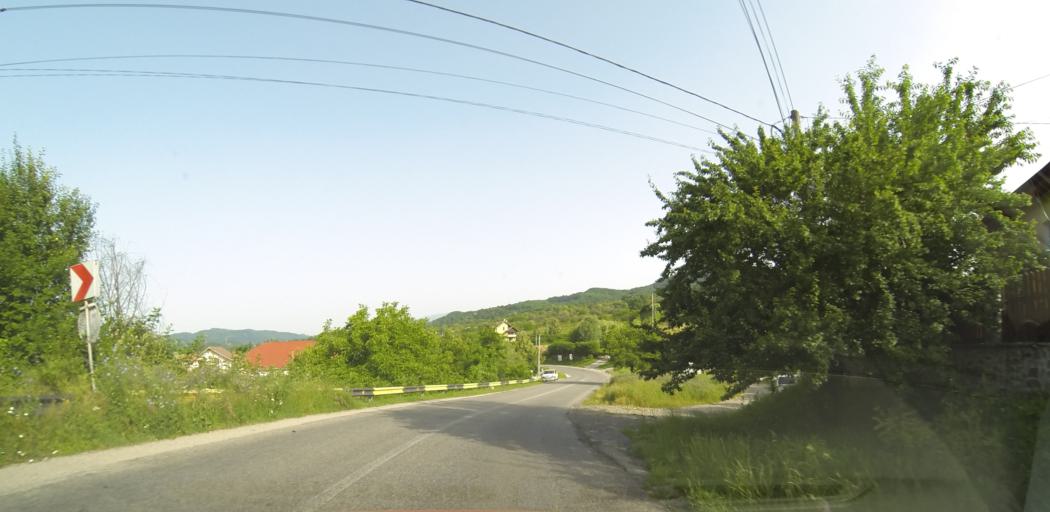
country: RO
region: Valcea
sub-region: Comuna Vladesti
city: Vladesti
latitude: 45.1237
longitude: 24.2876
